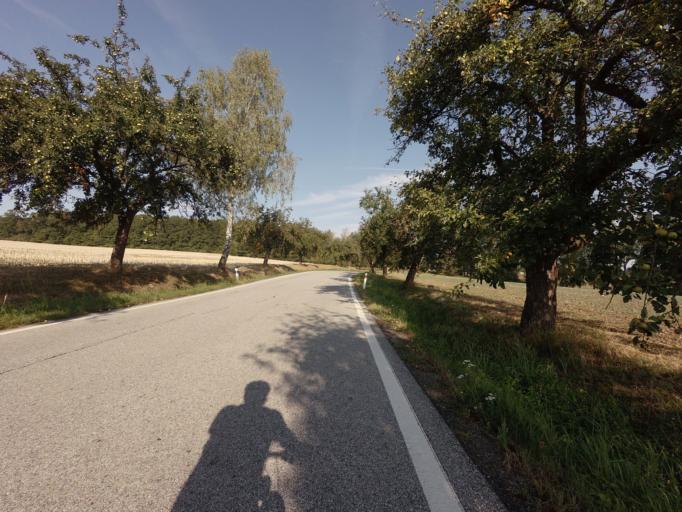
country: CZ
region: Jihocesky
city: Tyn nad Vltavou
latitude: 49.2579
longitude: 14.4151
